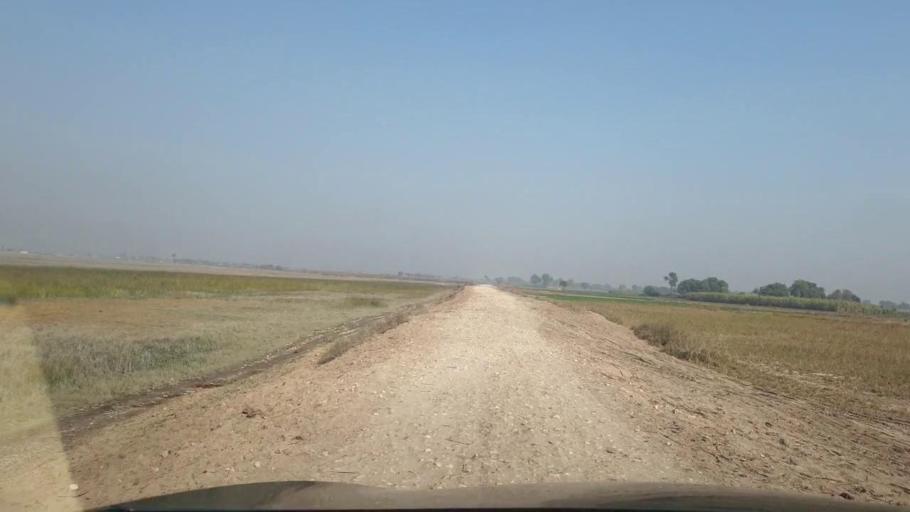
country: PK
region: Sindh
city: Ubauro
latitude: 28.1267
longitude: 69.7494
